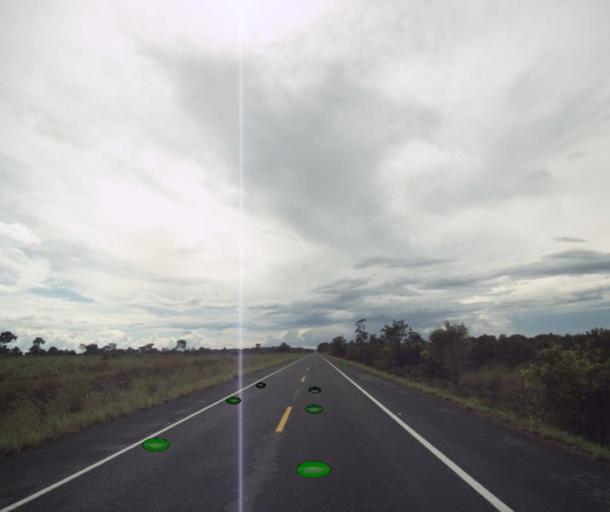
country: BR
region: Goias
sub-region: Sao Miguel Do Araguaia
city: Sao Miguel do Araguaia
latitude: -13.2653
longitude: -50.5127
